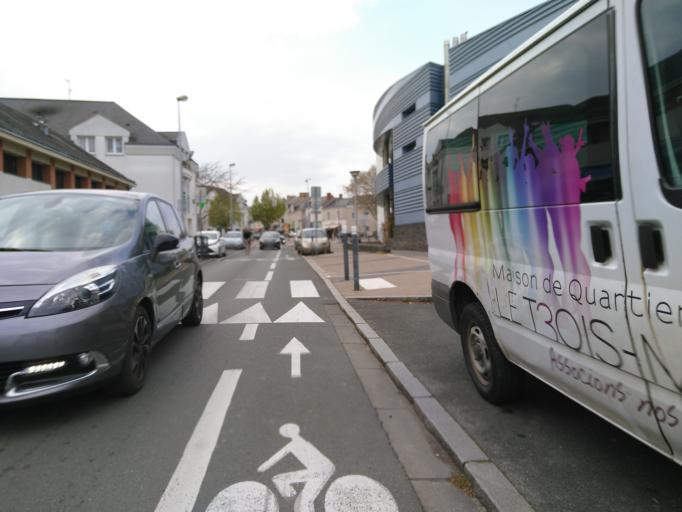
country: FR
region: Pays de la Loire
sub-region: Departement de Maine-et-Loire
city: Angers
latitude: 47.4524
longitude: -0.5254
